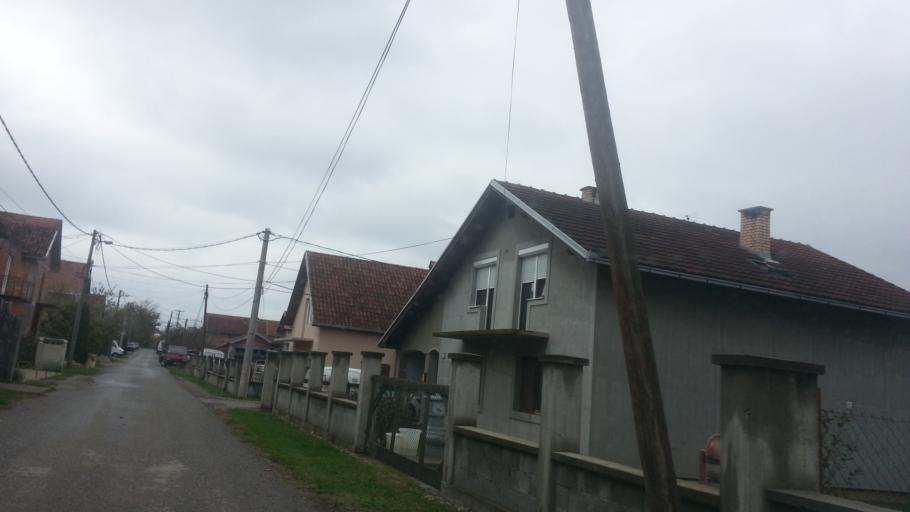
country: RS
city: Novi Banovci
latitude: 44.9186
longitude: 20.2819
